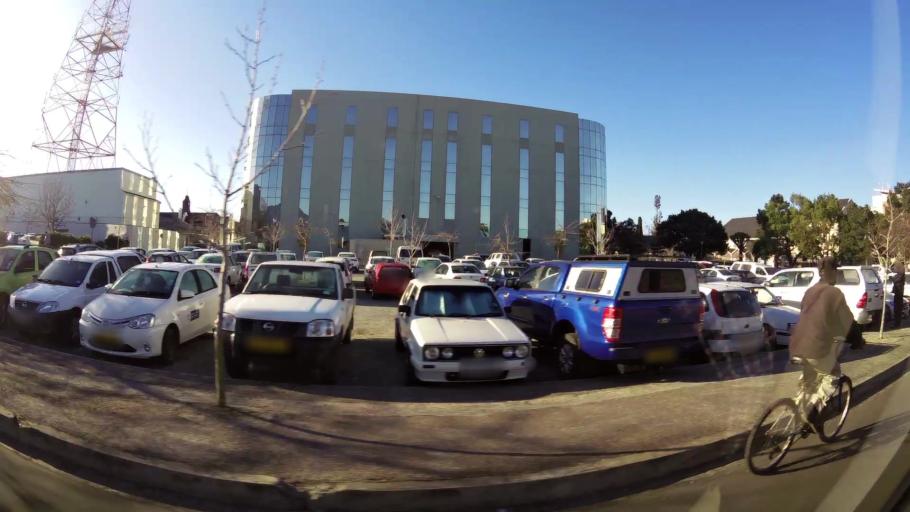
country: ZA
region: Western Cape
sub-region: Eden District Municipality
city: George
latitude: -33.9596
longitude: 22.4538
